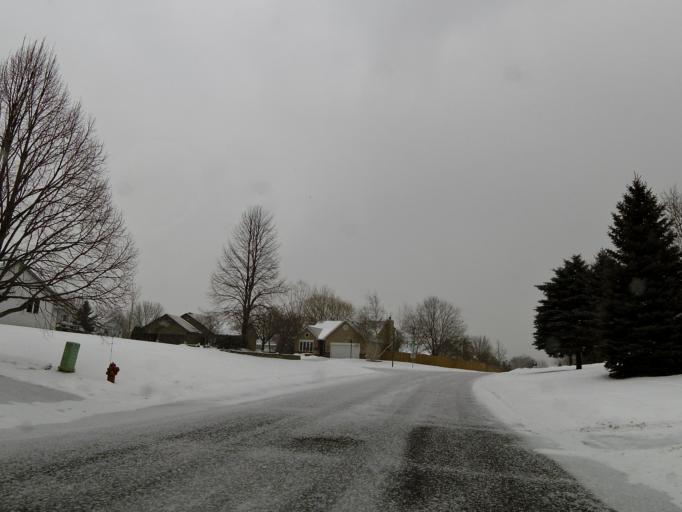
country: US
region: Minnesota
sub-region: Washington County
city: Woodbury
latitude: 44.9333
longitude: -92.9241
